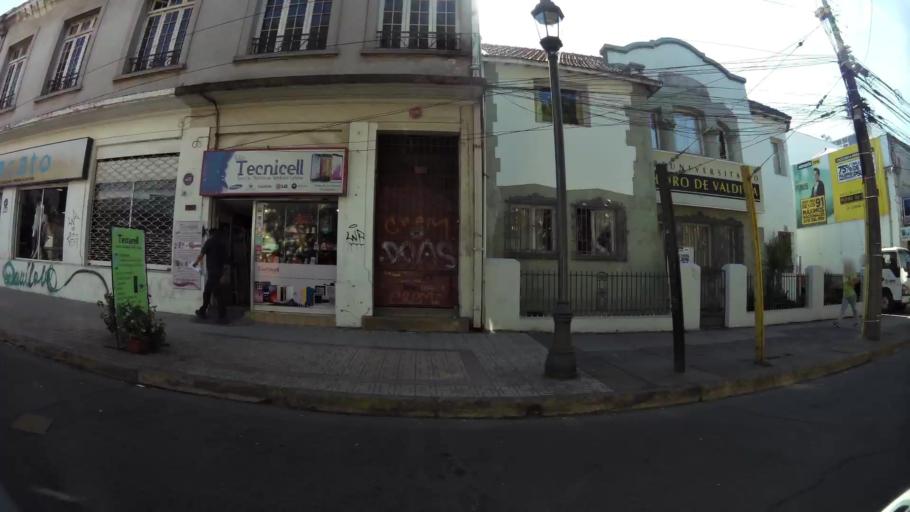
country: CL
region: Maule
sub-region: Provincia de Talca
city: Talca
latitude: -35.4269
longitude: -71.6626
